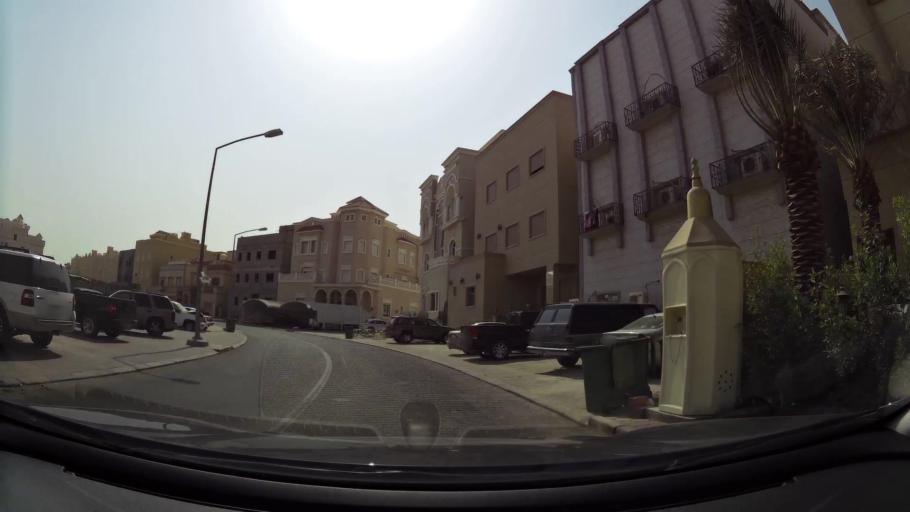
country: KW
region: Muhafazat al Jahra'
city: Al Jahra'
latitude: 29.3229
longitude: 47.7362
